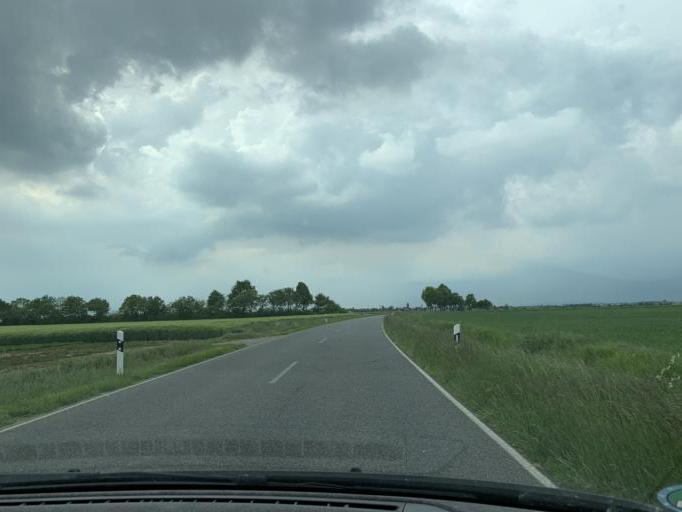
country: DE
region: North Rhine-Westphalia
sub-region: Regierungsbezirk Koln
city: Vettweiss
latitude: 50.7489
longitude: 6.5782
